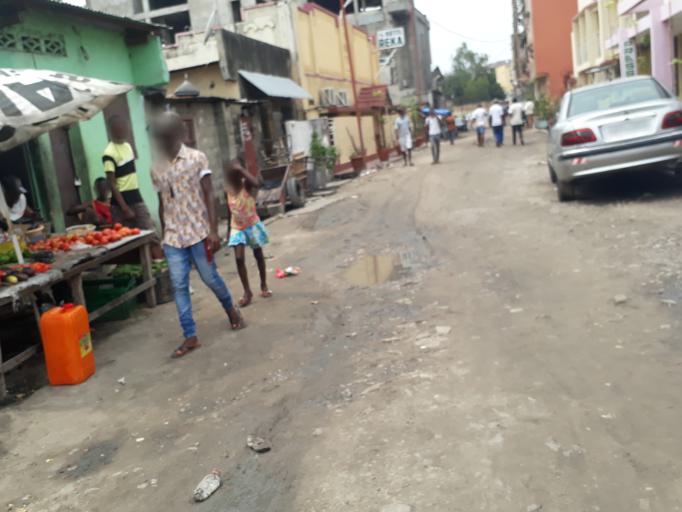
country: CD
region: Kinshasa
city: Kinshasa
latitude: -4.3094
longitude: 15.3208
